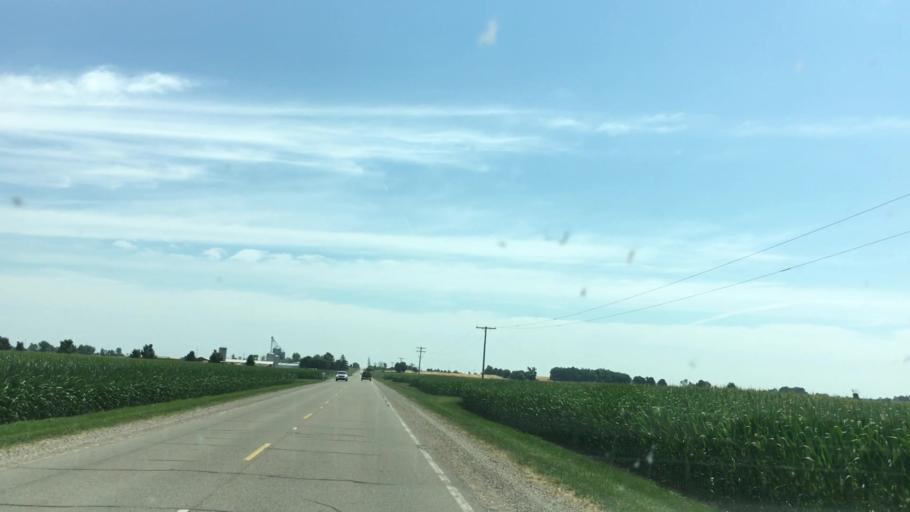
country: US
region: Michigan
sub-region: Sanilac County
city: Brown City
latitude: 43.2556
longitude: -83.0441
